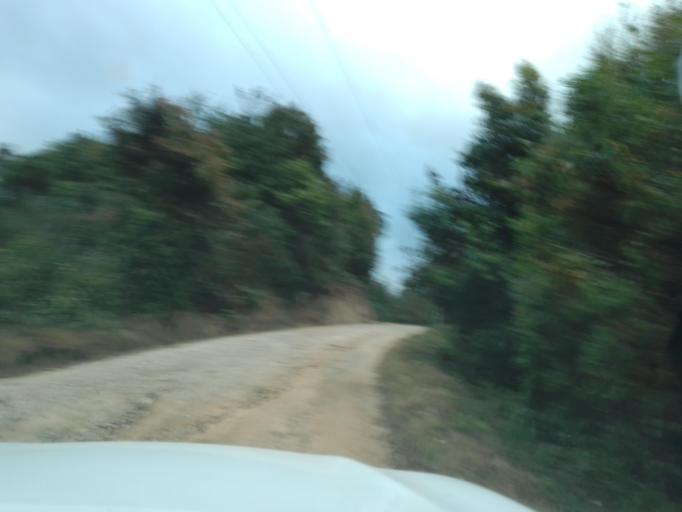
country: MX
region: Chiapas
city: Motozintla de Mendoza
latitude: 15.2129
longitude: -92.2278
